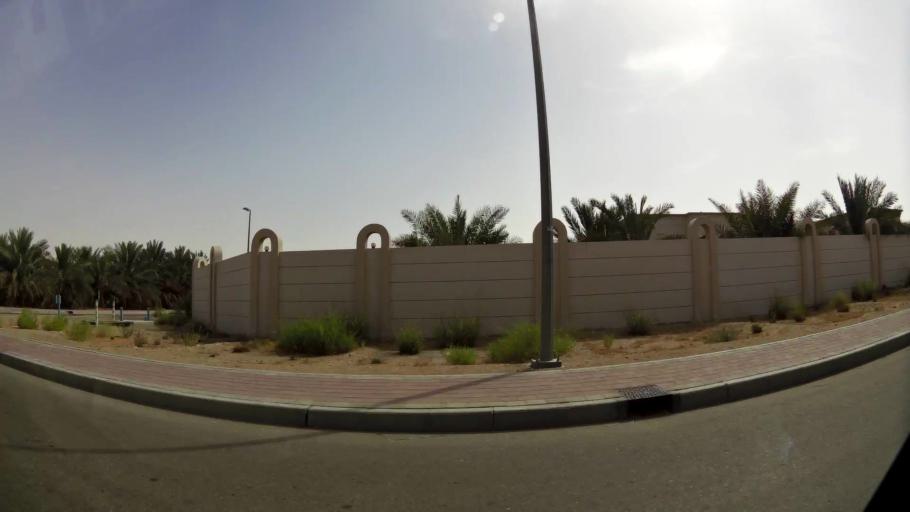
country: AE
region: Abu Dhabi
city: Al Ain
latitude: 24.1680
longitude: 55.6938
